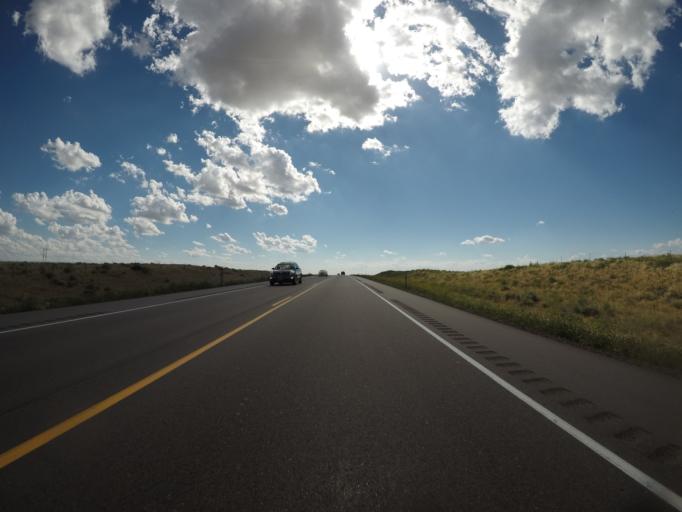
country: US
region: Colorado
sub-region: Logan County
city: Sterling
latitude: 40.6313
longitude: -103.1316
